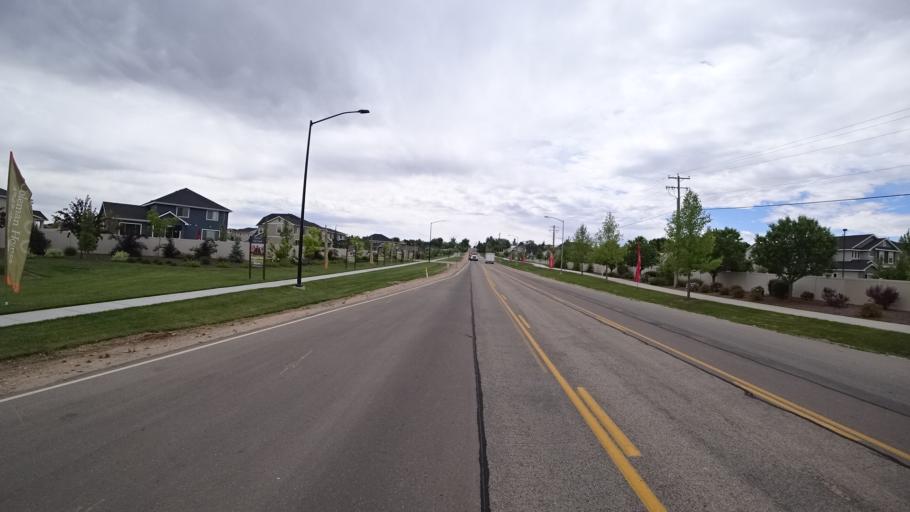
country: US
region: Idaho
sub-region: Ada County
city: Meridian
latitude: 43.5862
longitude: -116.4137
